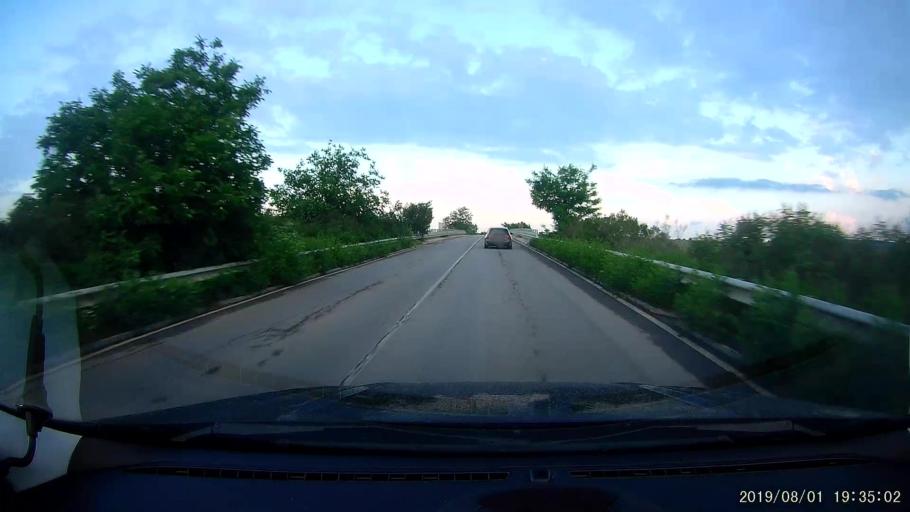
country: BG
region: Burgas
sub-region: Obshtina Sungurlare
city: Sungurlare
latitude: 42.7655
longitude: 26.8804
